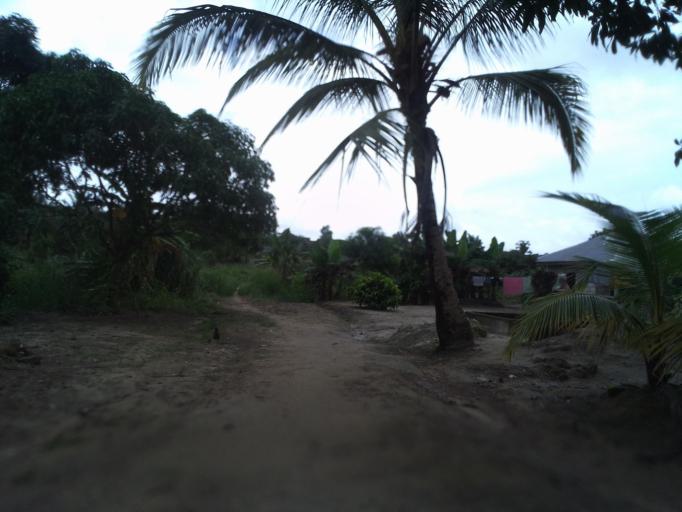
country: SL
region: Eastern Province
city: Kenema
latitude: 7.8470
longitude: -11.1840
